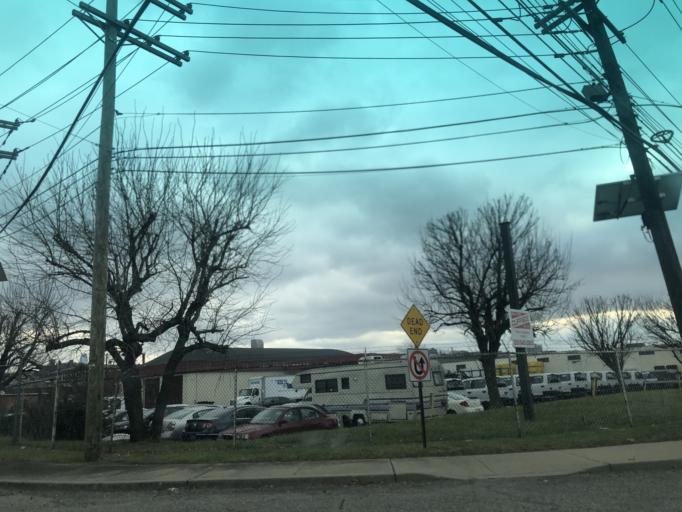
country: US
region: New Jersey
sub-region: Hudson County
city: Union City
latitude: 40.7845
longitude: -74.0381
